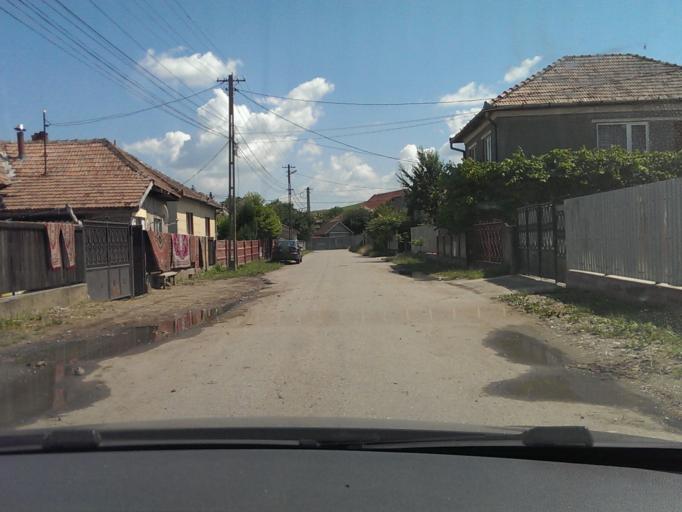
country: RO
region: Cluj
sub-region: Comuna Apahida
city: Apahida
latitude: 46.7968
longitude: 23.7466
